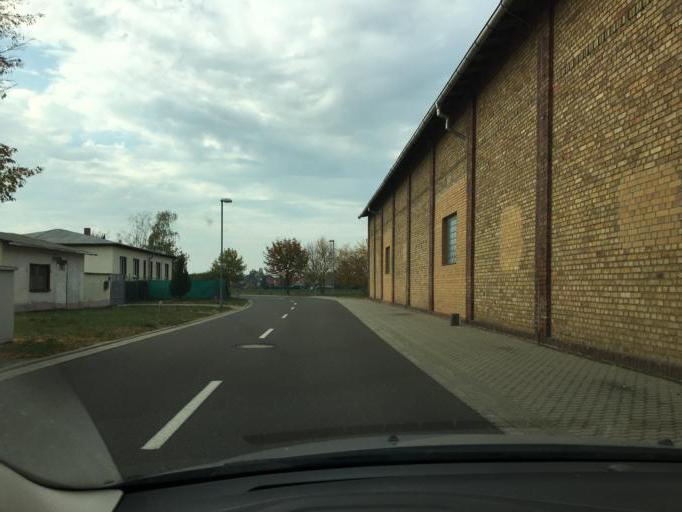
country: DE
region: Saxony
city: Zwochau
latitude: 51.4997
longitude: 12.2404
